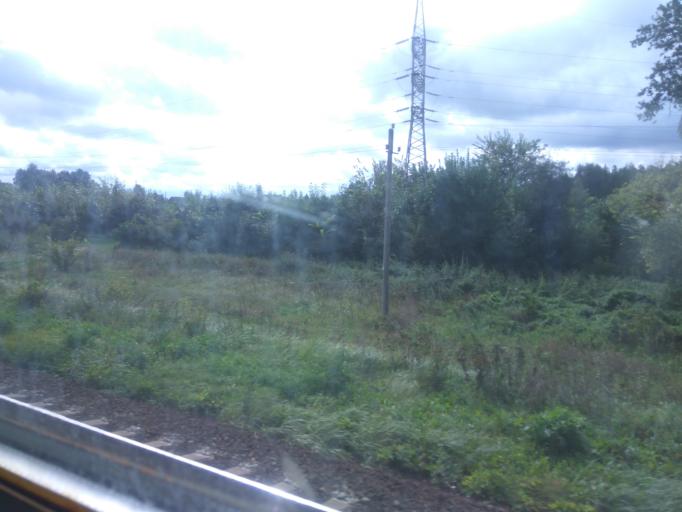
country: RU
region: Moskovskaya
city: Malyshevo
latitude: 55.4850
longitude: 38.3963
